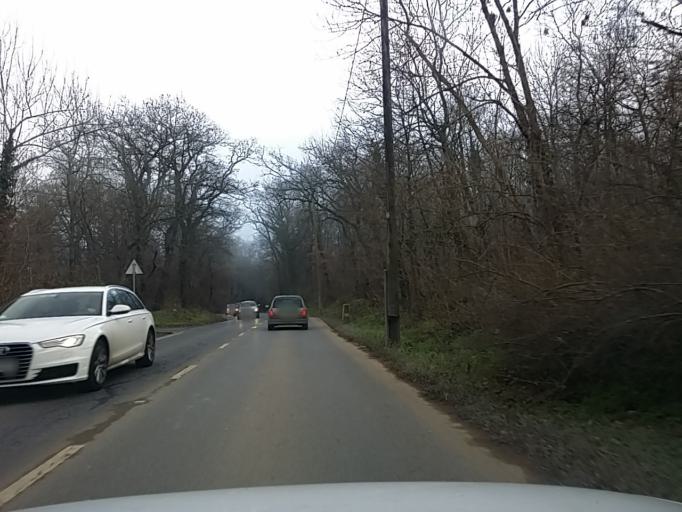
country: HU
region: Pest
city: Budakeszi
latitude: 47.5464
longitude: 18.9403
